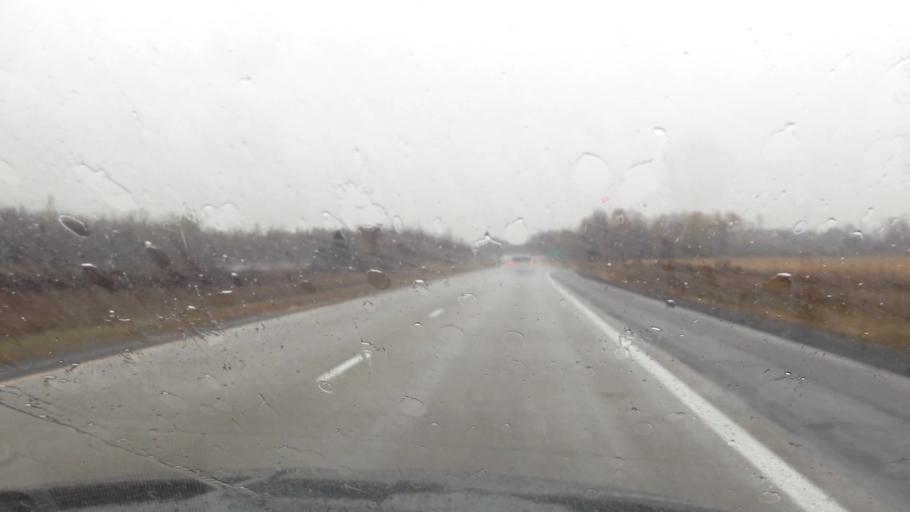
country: CA
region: Ontario
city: Hawkesbury
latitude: 45.4298
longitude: -74.7521
